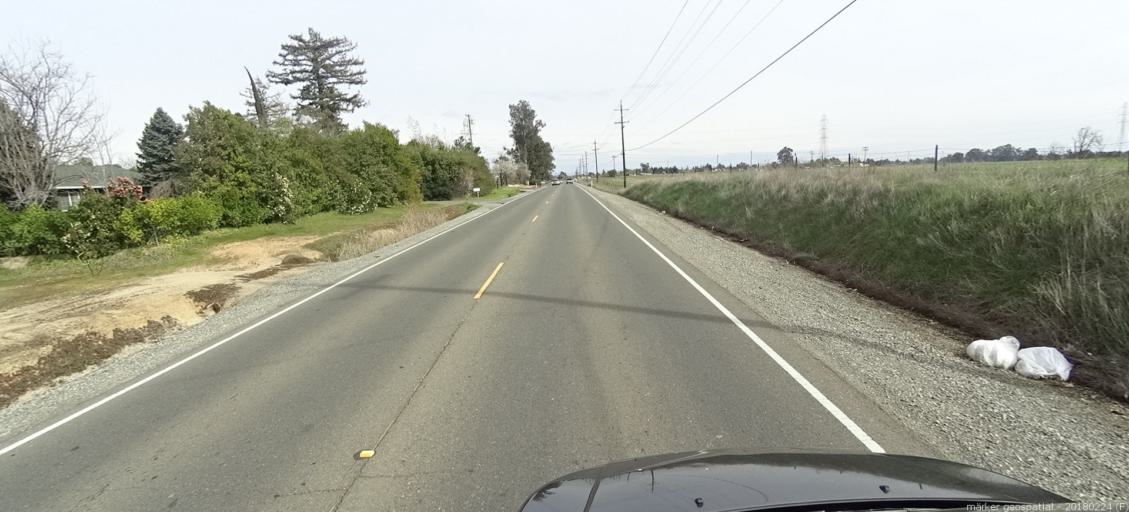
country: US
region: California
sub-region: Sacramento County
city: Rio Linda
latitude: 38.7144
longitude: -121.4350
